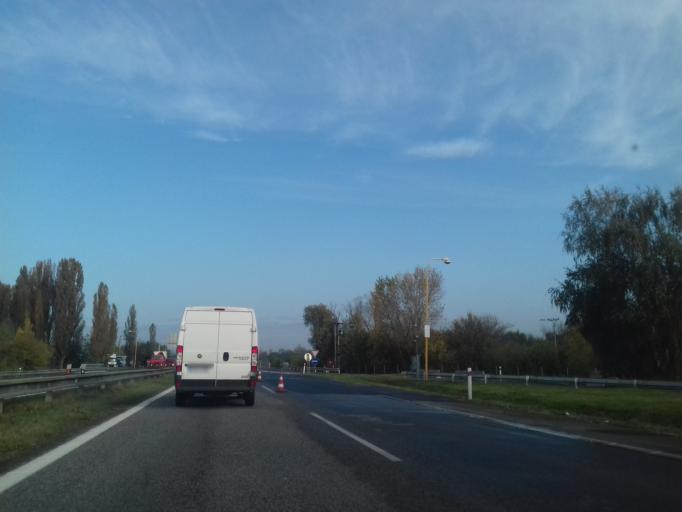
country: SK
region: Bratislavsky
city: Stupava
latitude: 48.2604
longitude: 17.0100
